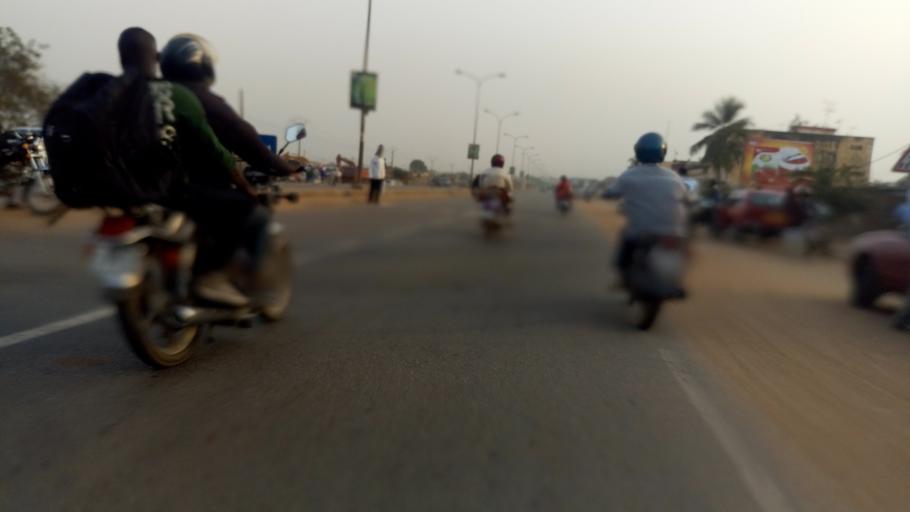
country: TG
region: Maritime
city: Lome
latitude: 6.2536
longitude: 1.2087
